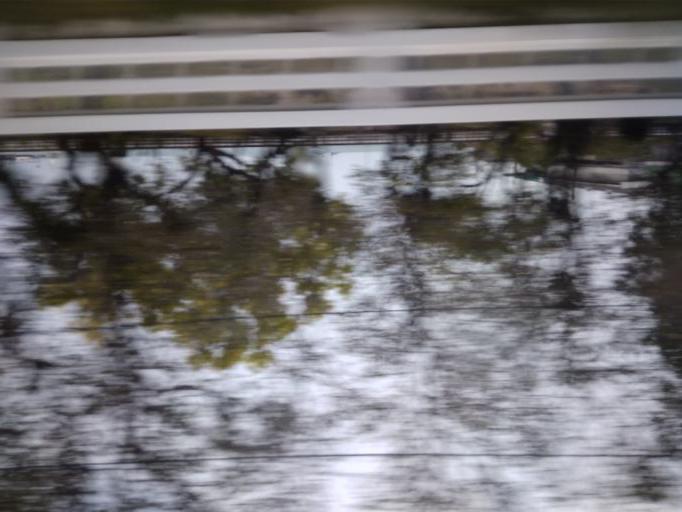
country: TH
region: Phuket
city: Mueang Phuket
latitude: 7.8276
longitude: 98.4025
